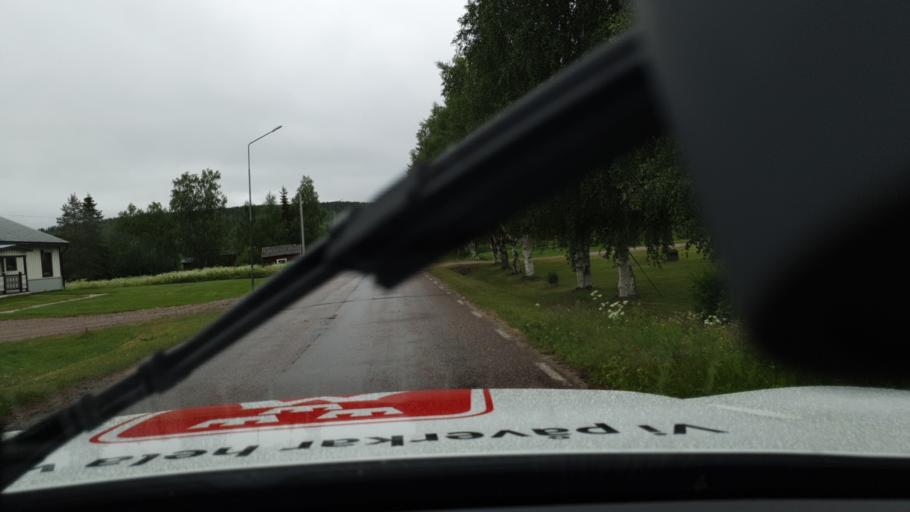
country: SE
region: Norrbotten
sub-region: Overtornea Kommun
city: OEvertornea
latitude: 66.4194
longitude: 23.6083
